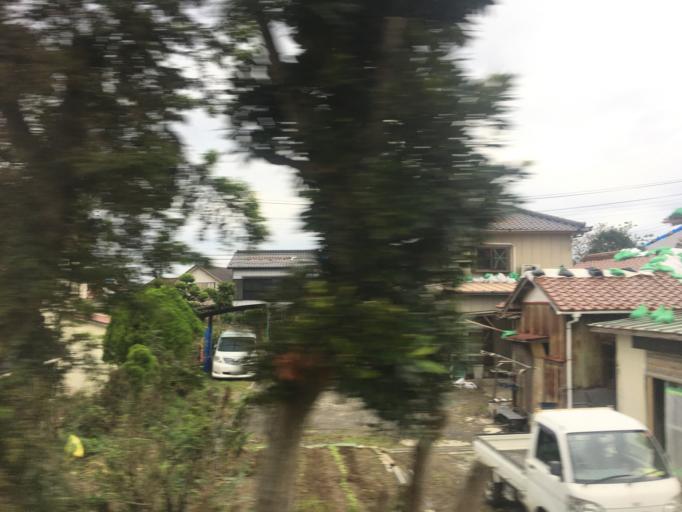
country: JP
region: Chiba
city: Tateyama
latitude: 35.1173
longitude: 139.8323
